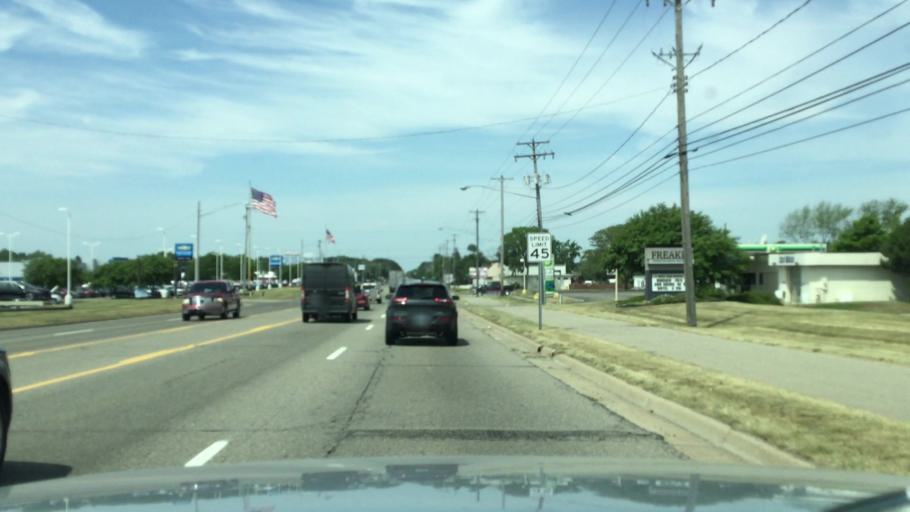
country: US
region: Michigan
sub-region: Genesee County
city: Swartz Creek
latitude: 43.0021
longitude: -83.7759
